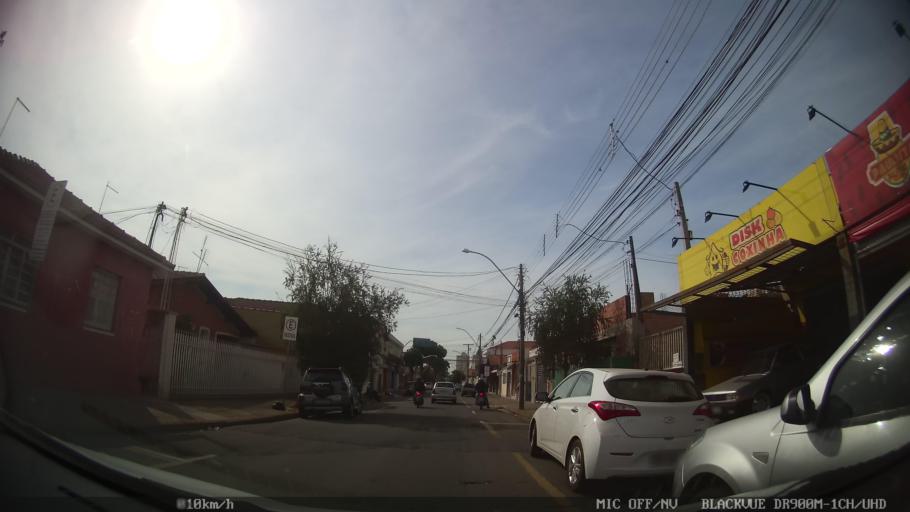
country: BR
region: Sao Paulo
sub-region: Piracicaba
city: Piracicaba
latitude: -22.7377
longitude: -47.6576
